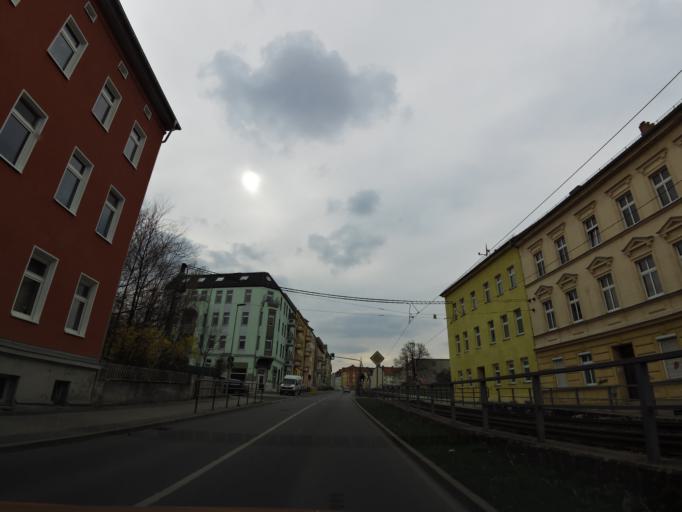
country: DE
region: Brandenburg
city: Frankfurt (Oder)
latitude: 52.3333
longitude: 14.5334
